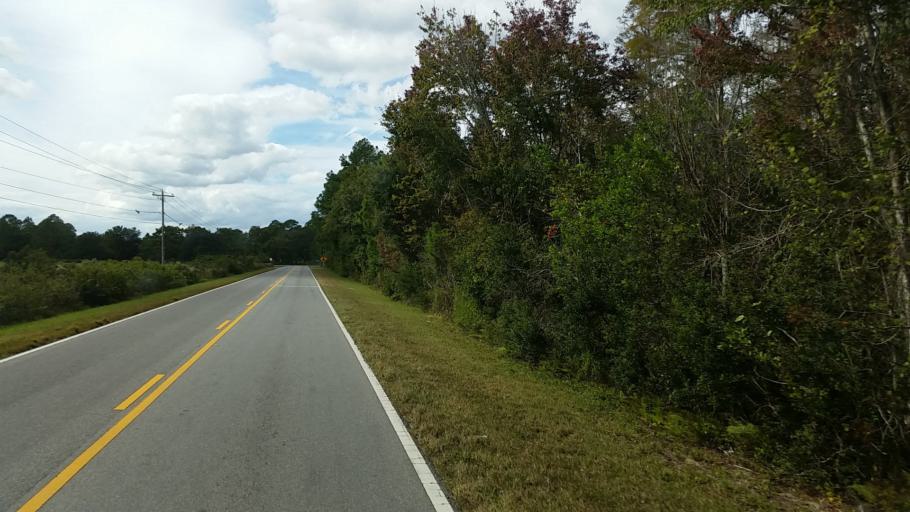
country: US
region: Florida
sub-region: Lake County
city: Four Corners
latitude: 28.3763
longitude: -81.8196
